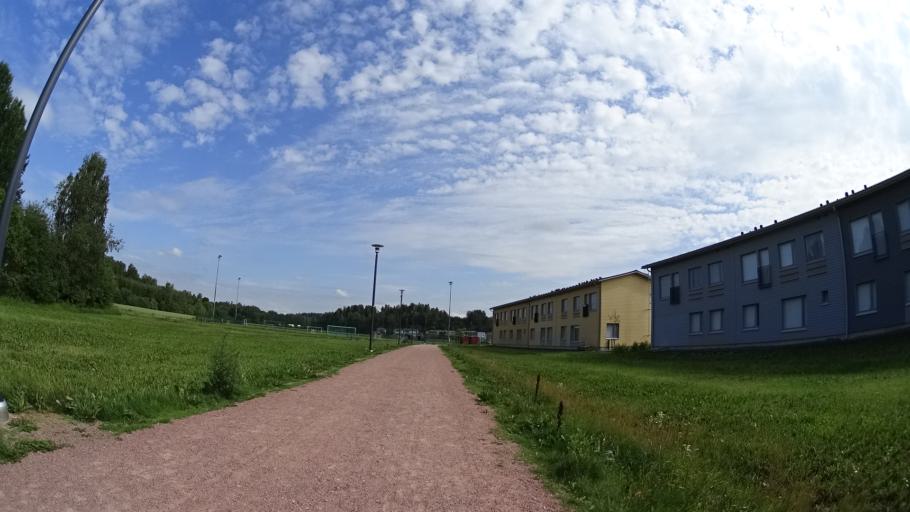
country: FI
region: Uusimaa
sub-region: Helsinki
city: Espoo
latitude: 60.1904
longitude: 24.5846
